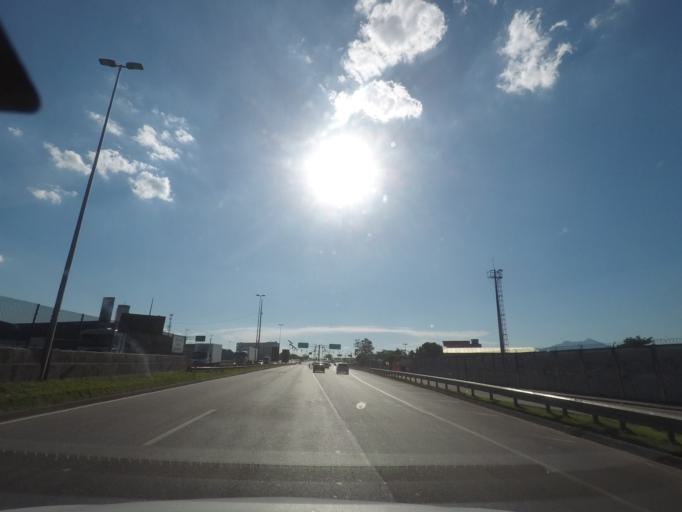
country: BR
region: Rio de Janeiro
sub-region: Duque De Caxias
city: Duque de Caxias
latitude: -22.6713
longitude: -43.2784
